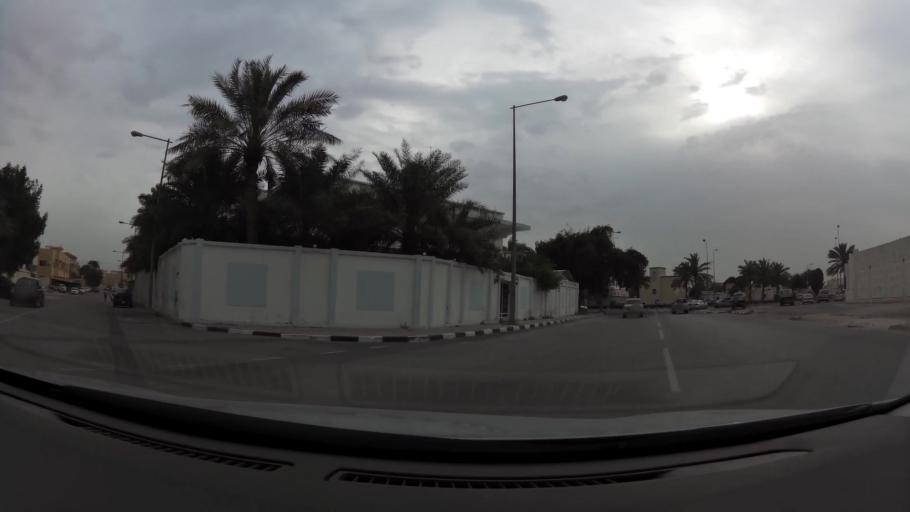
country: QA
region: Baladiyat ad Dawhah
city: Doha
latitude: 25.3128
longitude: 51.4881
